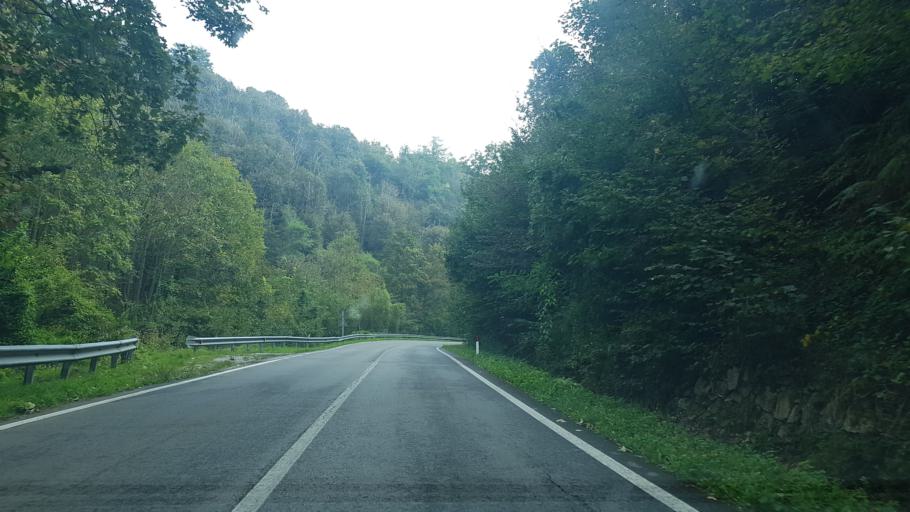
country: IT
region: Piedmont
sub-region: Provincia di Cuneo
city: Chiusa di Pesio
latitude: 44.3165
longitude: 7.6890
